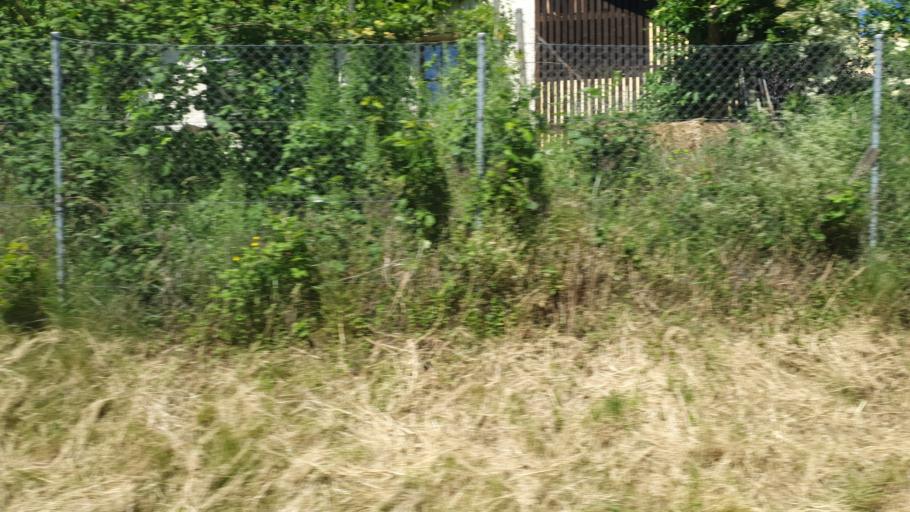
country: CH
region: Fribourg
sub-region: Sarine District
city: Givisiez
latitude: 46.8445
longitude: 7.1388
